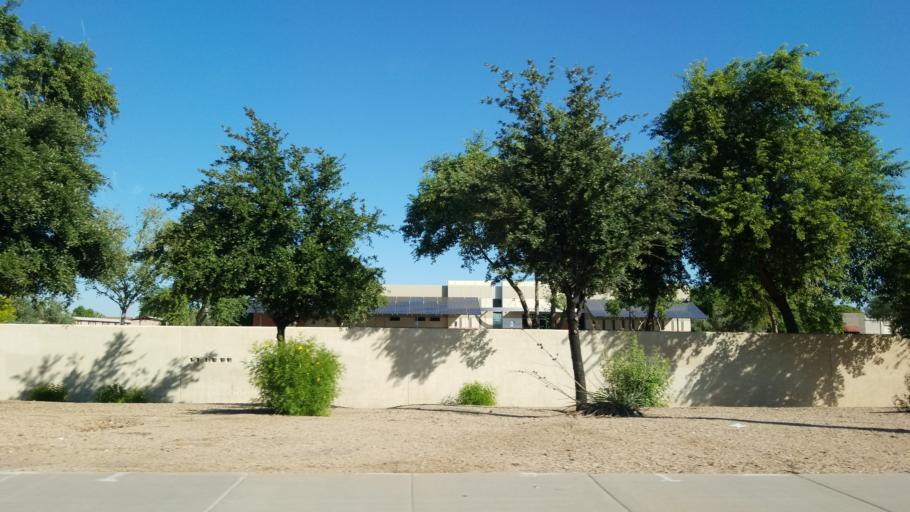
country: US
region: Arizona
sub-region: Maricopa County
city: Glendale
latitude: 33.5242
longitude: -112.1836
